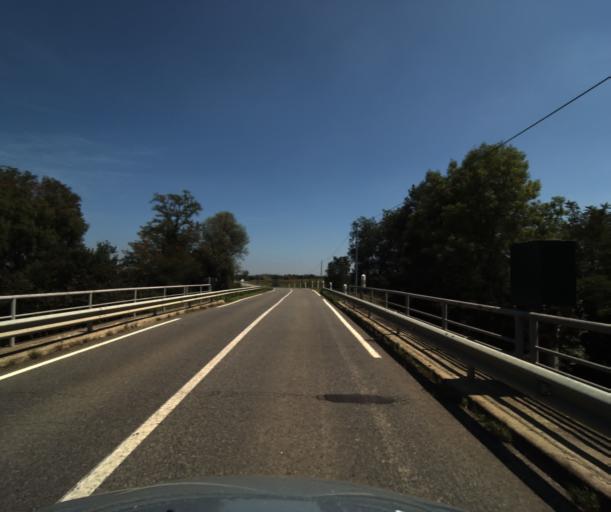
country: FR
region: Midi-Pyrenees
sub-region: Departement de la Haute-Garonne
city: Fonsorbes
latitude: 43.5047
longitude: 1.2435
